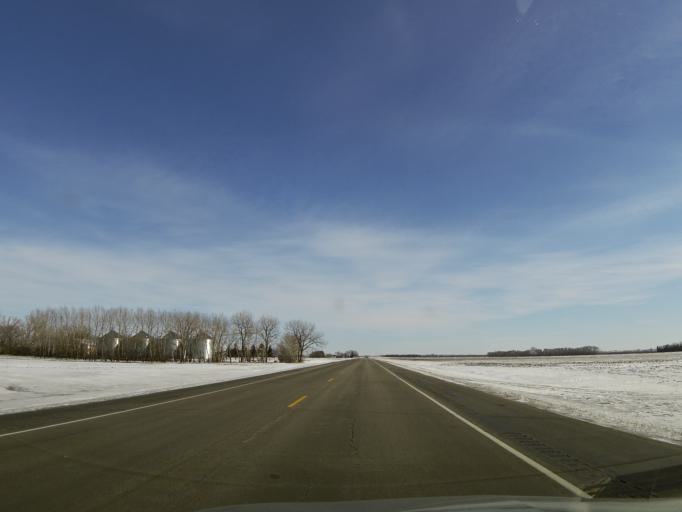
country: US
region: North Dakota
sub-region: Walsh County
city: Grafton
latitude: 48.4121
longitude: -97.2233
